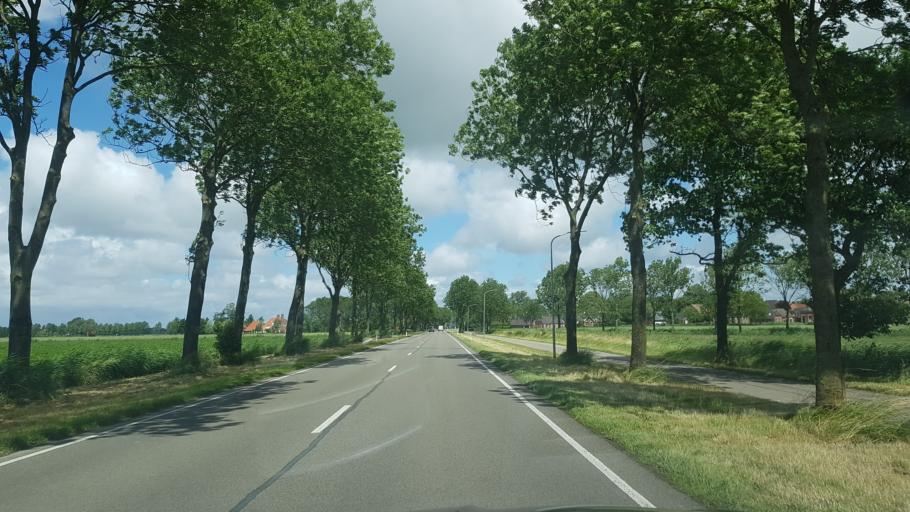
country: NL
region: Groningen
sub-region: Gemeente Winsum
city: Winsum
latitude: 53.3658
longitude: 6.5122
